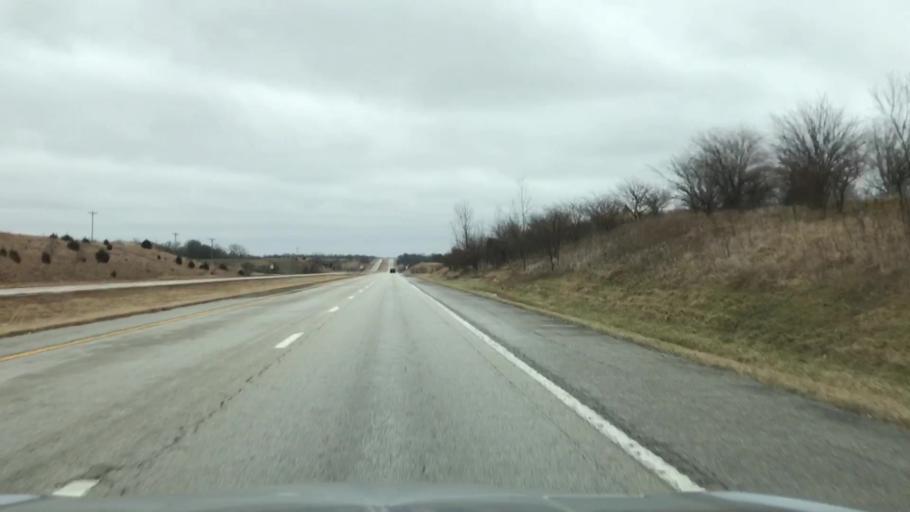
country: US
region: Missouri
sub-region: Clinton County
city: Cameron
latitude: 39.7507
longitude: -94.1335
